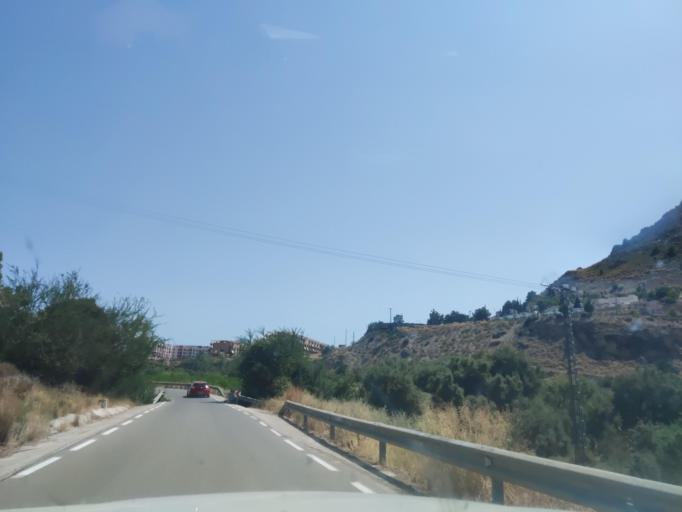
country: ES
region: Murcia
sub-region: Murcia
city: Archena
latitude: 38.1308
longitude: -1.3131
